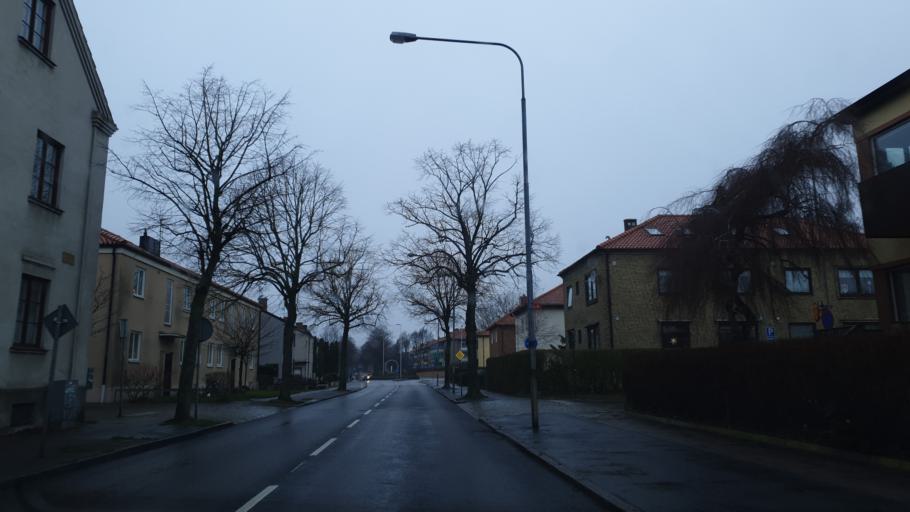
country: SE
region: Skane
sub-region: Trelleborgs Kommun
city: Trelleborg
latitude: 55.3783
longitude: 13.1692
